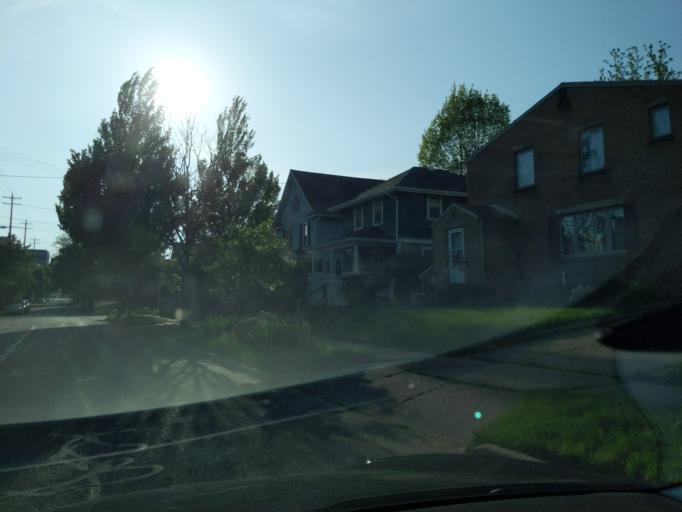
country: US
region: Michigan
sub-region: Ingham County
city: Lansing
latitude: 42.7347
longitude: -84.5284
